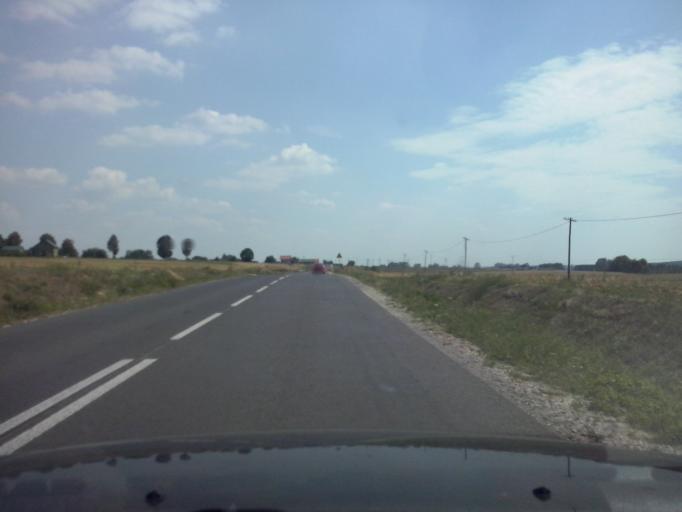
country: PL
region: Swietokrzyskie
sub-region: Powiat buski
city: Gnojno
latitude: 50.5886
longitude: 20.9008
